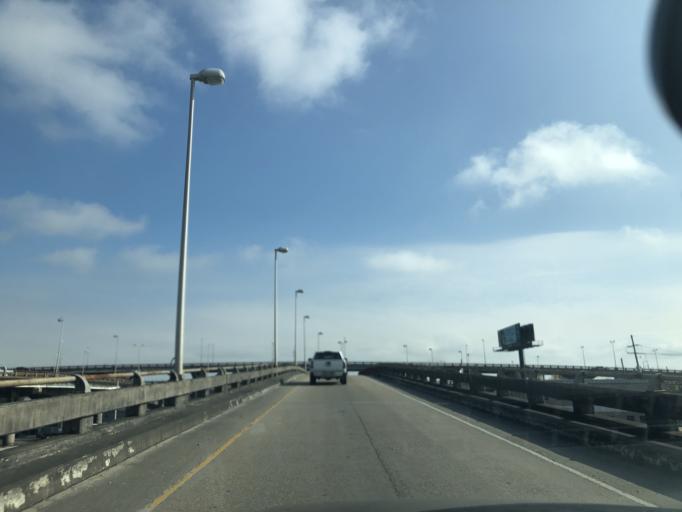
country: US
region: Louisiana
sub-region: Jefferson Parish
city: Metairie Terrace
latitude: 29.9746
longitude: -90.1583
